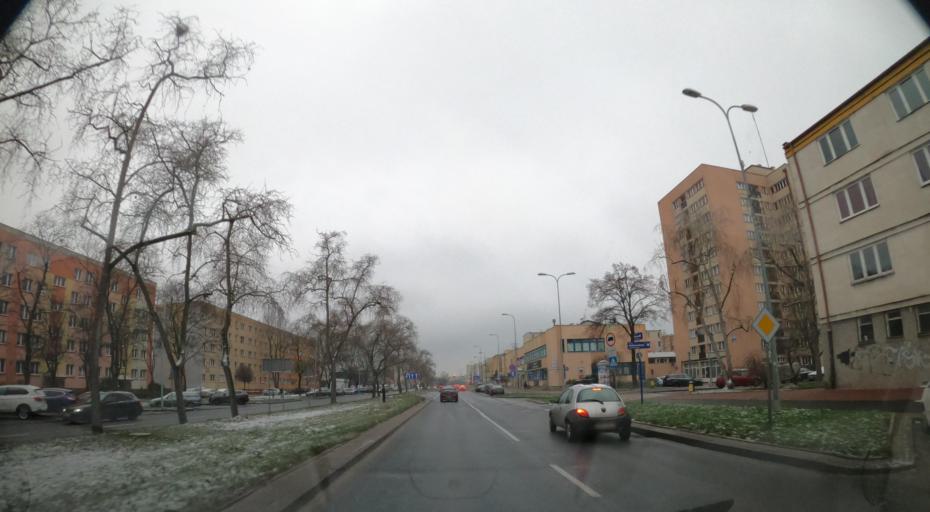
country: PL
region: Masovian Voivodeship
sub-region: Plock
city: Plock
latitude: 52.5486
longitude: 19.6975
